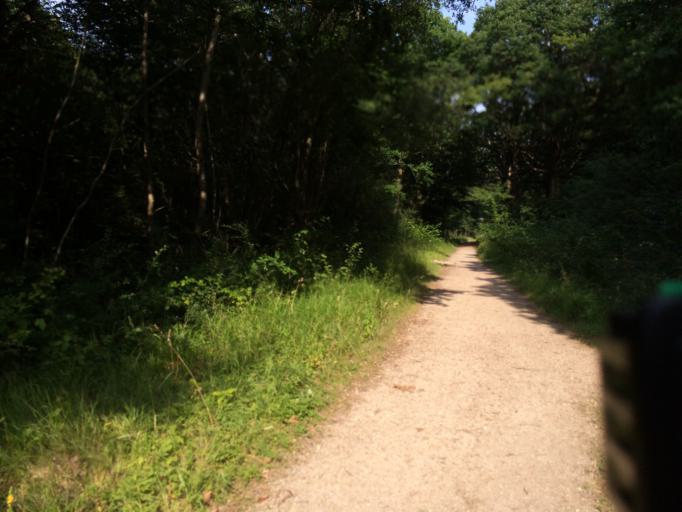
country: FR
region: Ile-de-France
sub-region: Departement de l'Essonne
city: Soisy-sur-Seine
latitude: 48.6685
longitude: 2.4575
